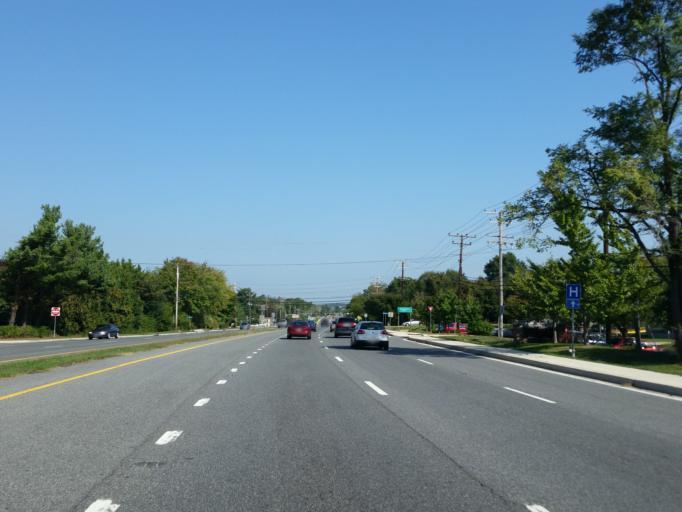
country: US
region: Maryland
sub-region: Prince George's County
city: South Laurel
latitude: 39.0770
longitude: -76.8485
